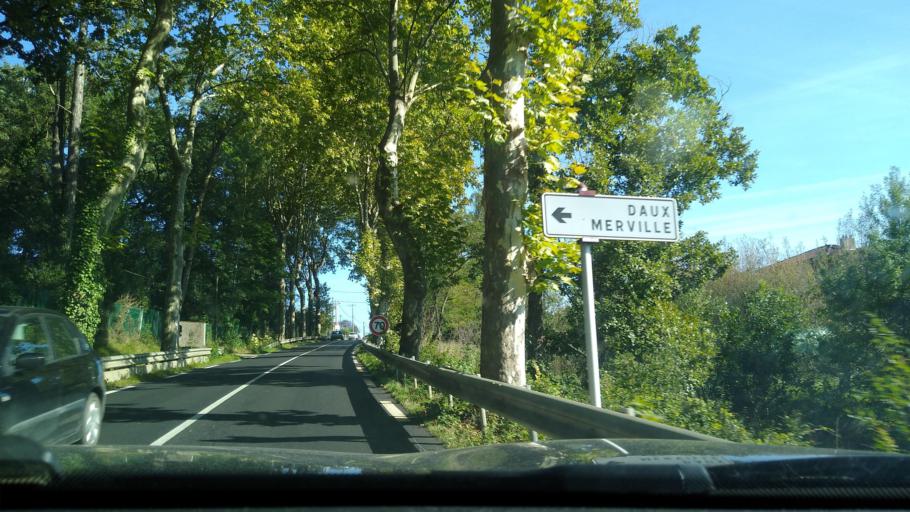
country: FR
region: Midi-Pyrenees
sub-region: Departement de la Haute-Garonne
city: Montaigut-sur-Save
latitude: 43.6879
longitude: 1.2395
